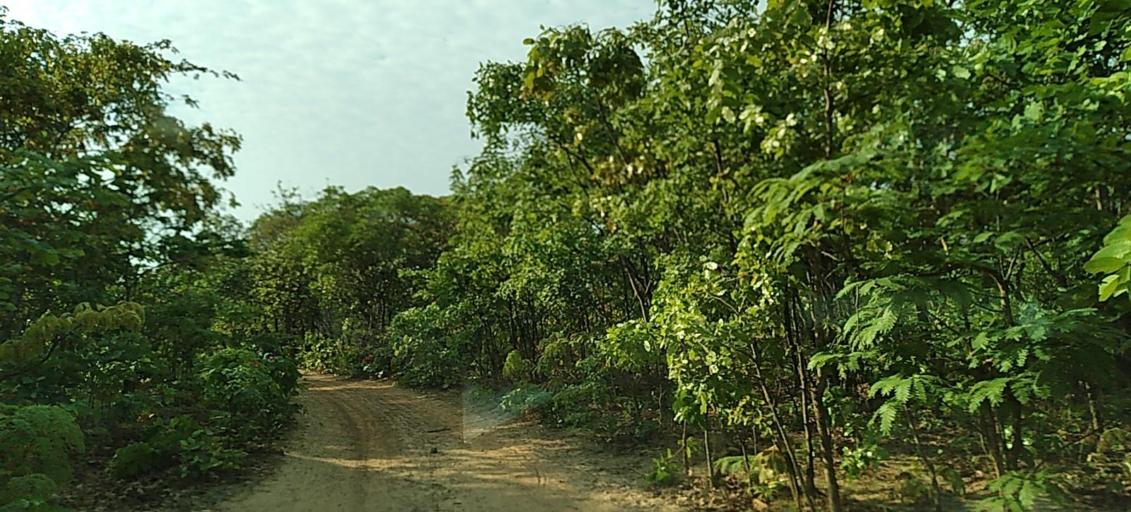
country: ZM
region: Copperbelt
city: Kalulushi
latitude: -12.9547
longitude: 27.6938
